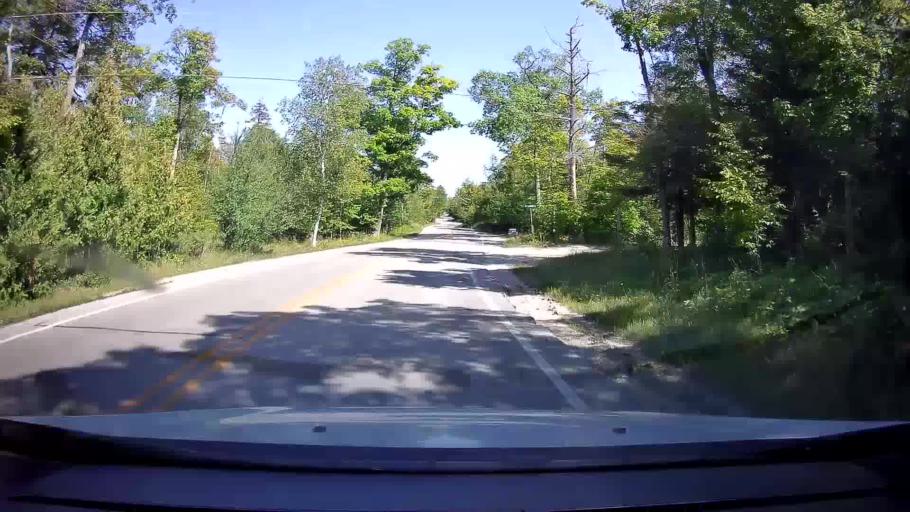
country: US
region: Michigan
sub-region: Delta County
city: Escanaba
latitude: 45.2893
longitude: -86.9932
